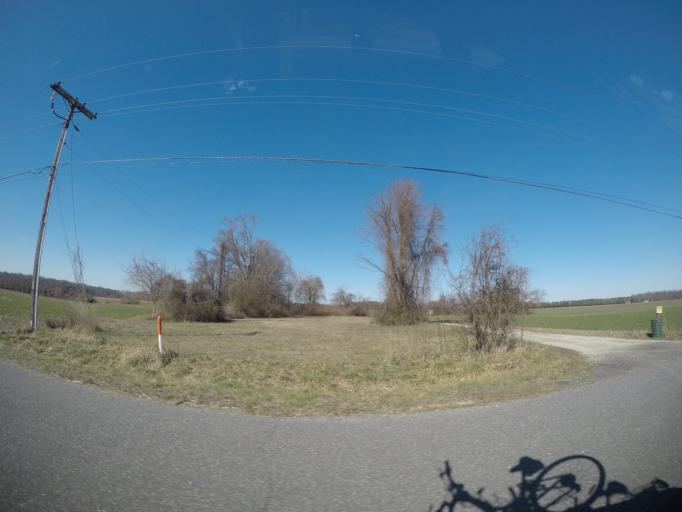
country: US
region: Delaware
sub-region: New Castle County
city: Townsend
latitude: 39.3542
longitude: -75.8366
